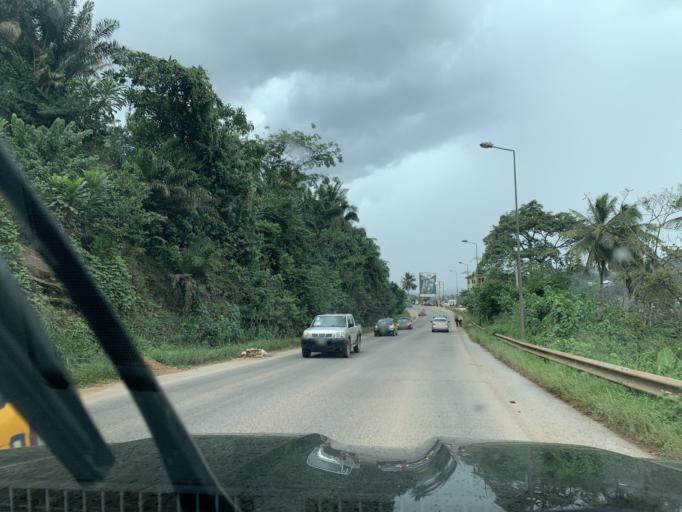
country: GH
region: Western
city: Tarkwa
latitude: 5.3181
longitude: -1.9878
